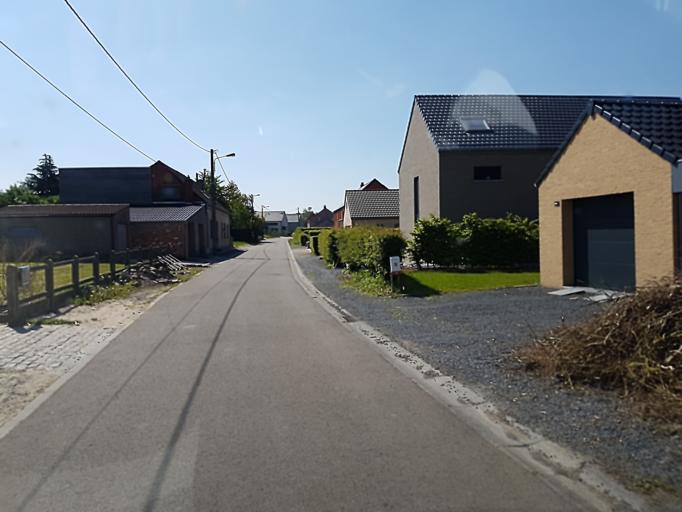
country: BE
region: Wallonia
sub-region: Province du Hainaut
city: Jurbise
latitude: 50.5114
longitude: 3.9056
